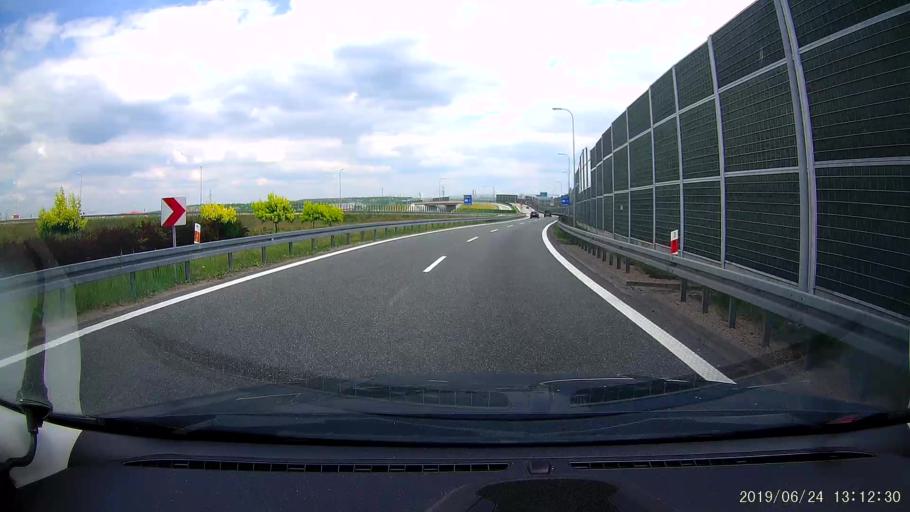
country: PL
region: Silesian Voivodeship
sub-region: Powiat gliwicki
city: Przyszowice
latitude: 50.2581
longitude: 18.7201
